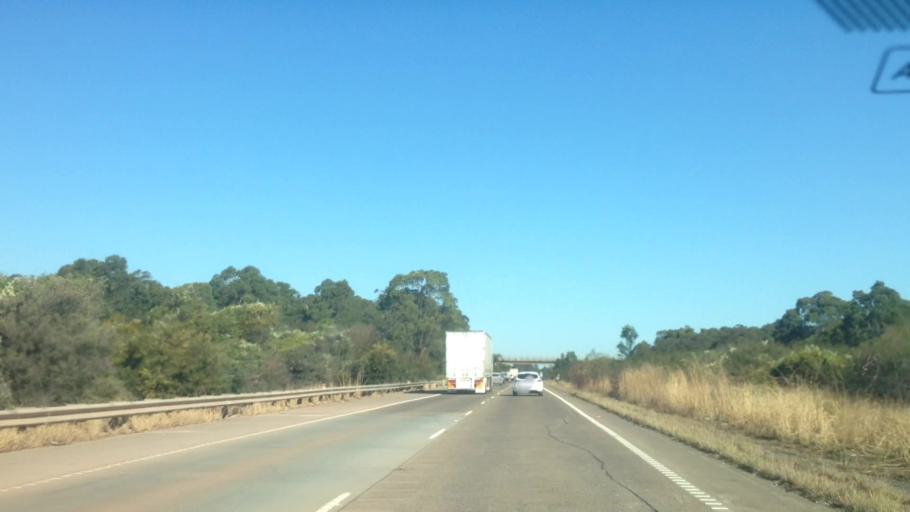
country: AU
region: New South Wales
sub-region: Wyong Shire
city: Charmhaven
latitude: -33.1777
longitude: 151.4672
